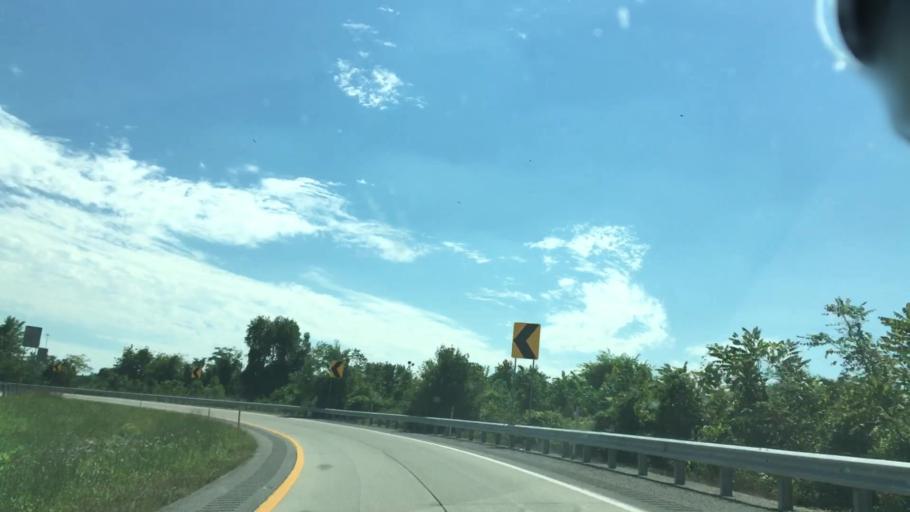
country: US
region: Kentucky
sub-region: Henderson County
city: Henderson
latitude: 37.8114
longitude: -87.5670
